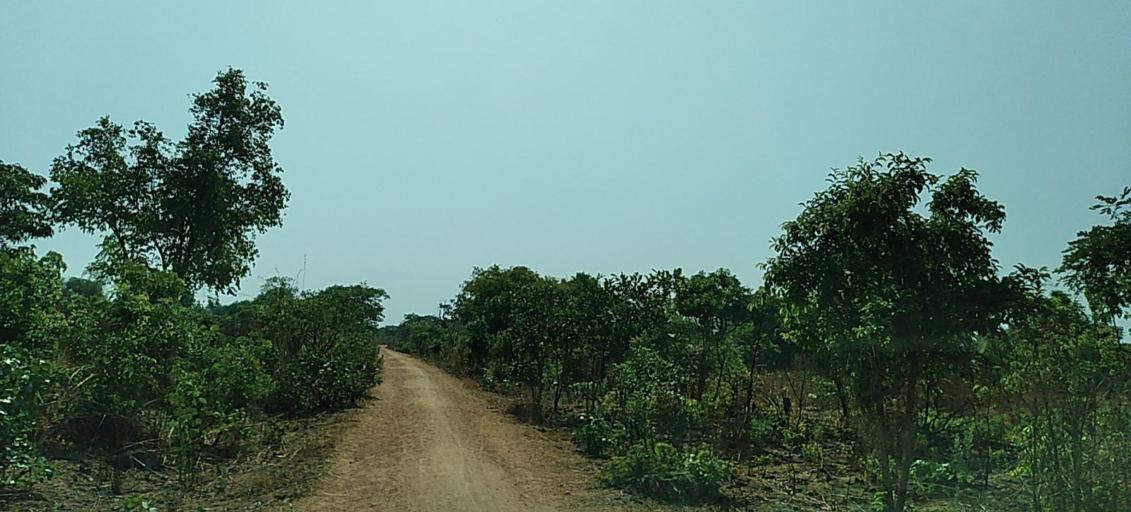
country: ZM
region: Copperbelt
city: Luanshya
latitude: -13.2817
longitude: 28.3182
